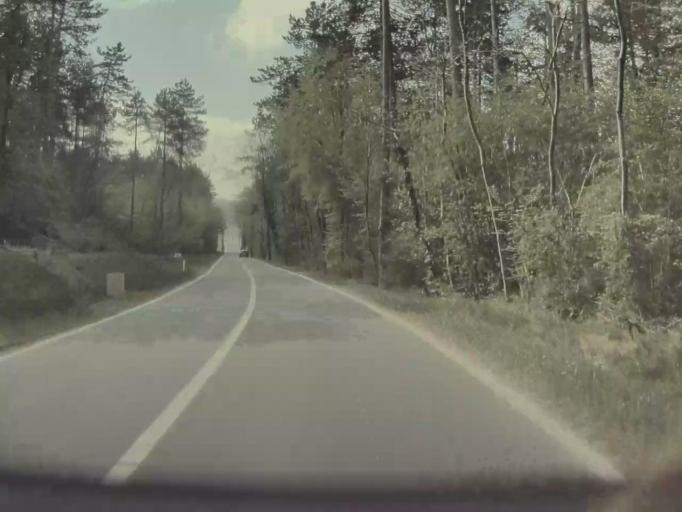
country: BE
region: Wallonia
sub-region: Province du Luxembourg
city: Tellin
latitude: 50.0994
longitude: 5.2309
